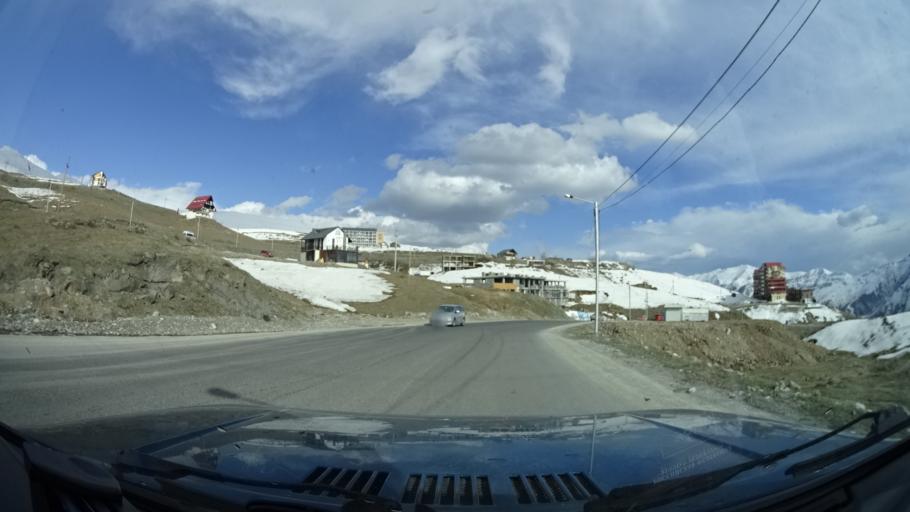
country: GE
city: Gudauri
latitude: 42.4710
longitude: 44.4791
